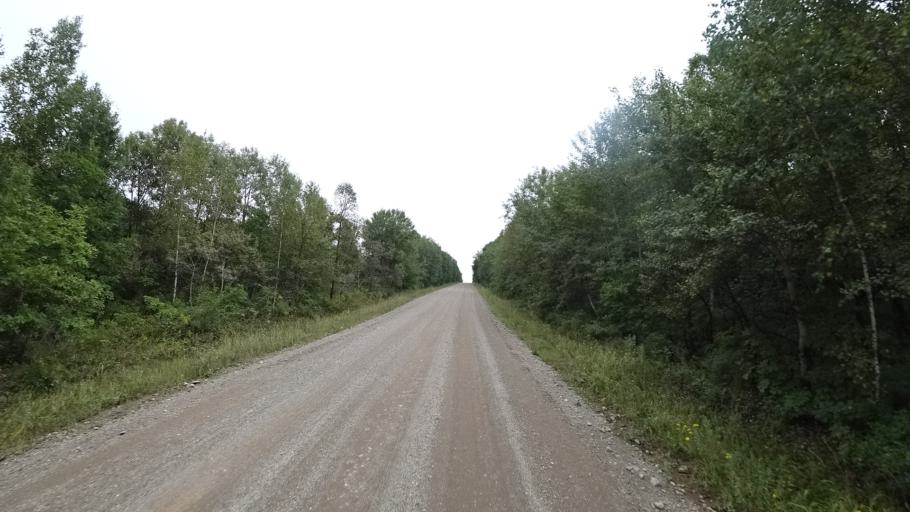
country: RU
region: Primorskiy
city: Ivanovka
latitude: 44.0259
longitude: 132.5168
